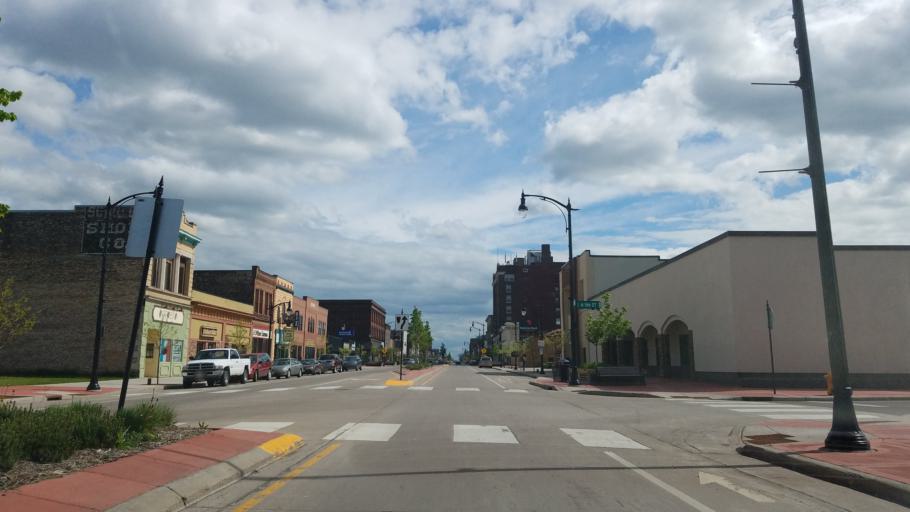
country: US
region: Wisconsin
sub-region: Douglas County
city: Superior
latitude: 46.7258
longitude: -92.1040
